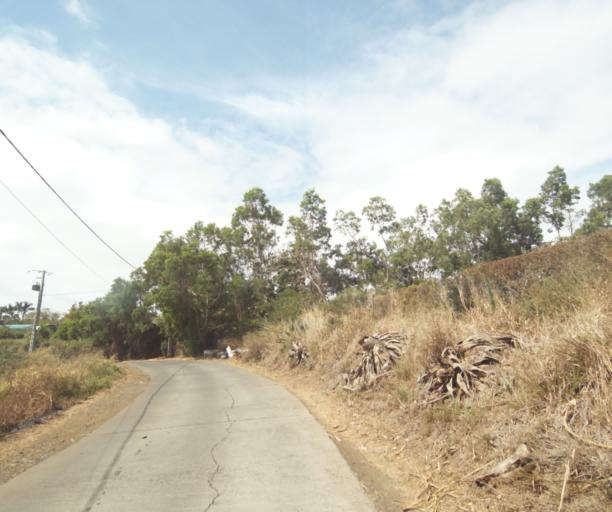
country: RE
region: Reunion
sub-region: Reunion
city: Trois-Bassins
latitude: -21.0645
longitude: 55.2644
